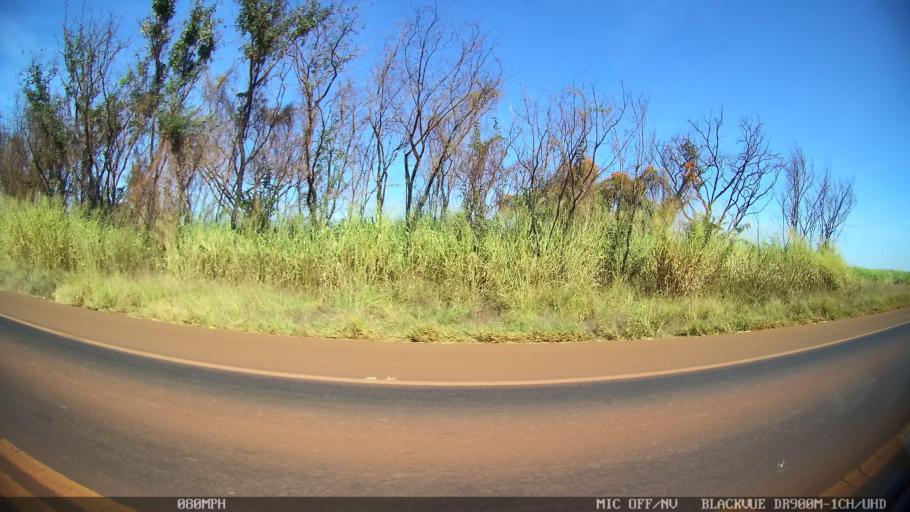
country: BR
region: Sao Paulo
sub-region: Sao Joaquim Da Barra
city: Sao Joaquim da Barra
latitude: -20.5440
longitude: -47.7875
